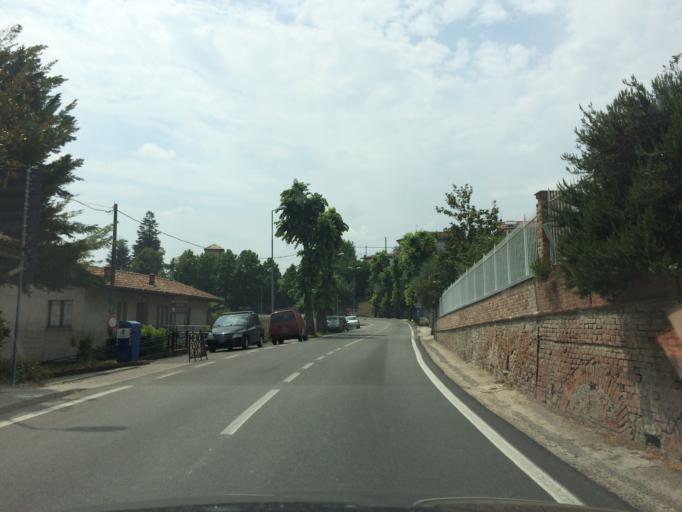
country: IT
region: Piedmont
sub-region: Provincia di Cuneo
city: Barolo
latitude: 44.6099
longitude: 7.9403
